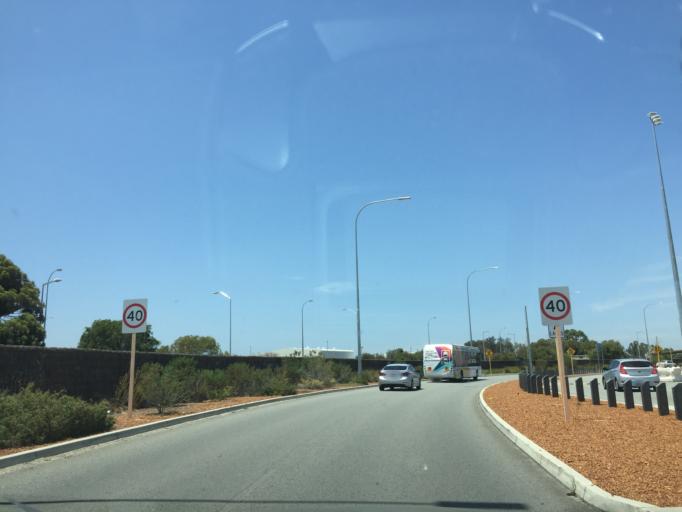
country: AU
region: Western Australia
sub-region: Belmont
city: Redcliffe
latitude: -31.9430
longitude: 115.9767
